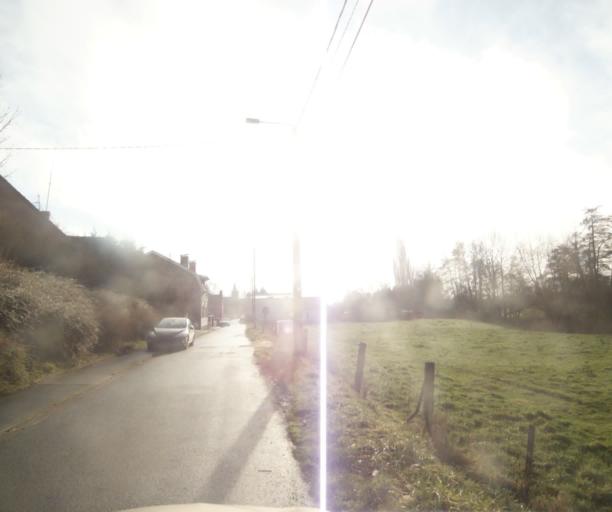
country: FR
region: Nord-Pas-de-Calais
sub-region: Departement du Nord
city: Thiant
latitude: 50.2902
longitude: 3.4540
